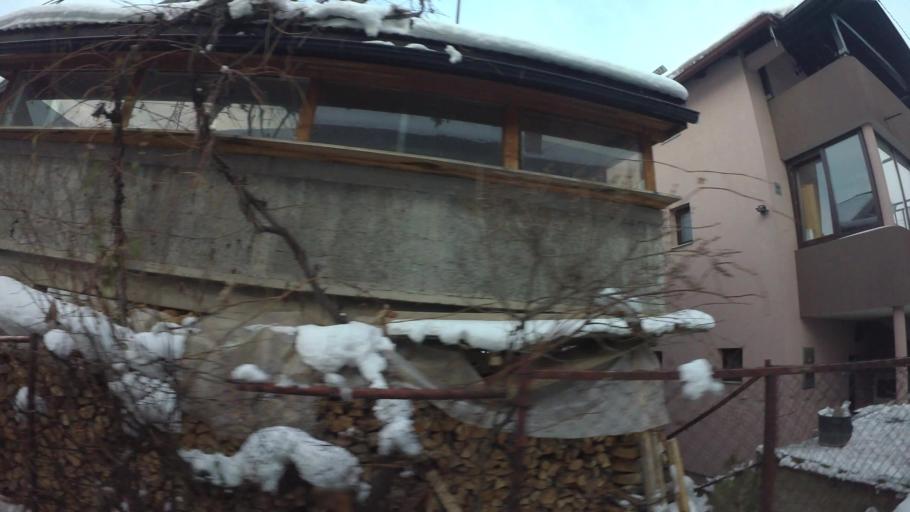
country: BA
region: Federation of Bosnia and Herzegovina
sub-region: Kanton Sarajevo
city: Sarajevo
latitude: 43.8399
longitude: 18.3568
